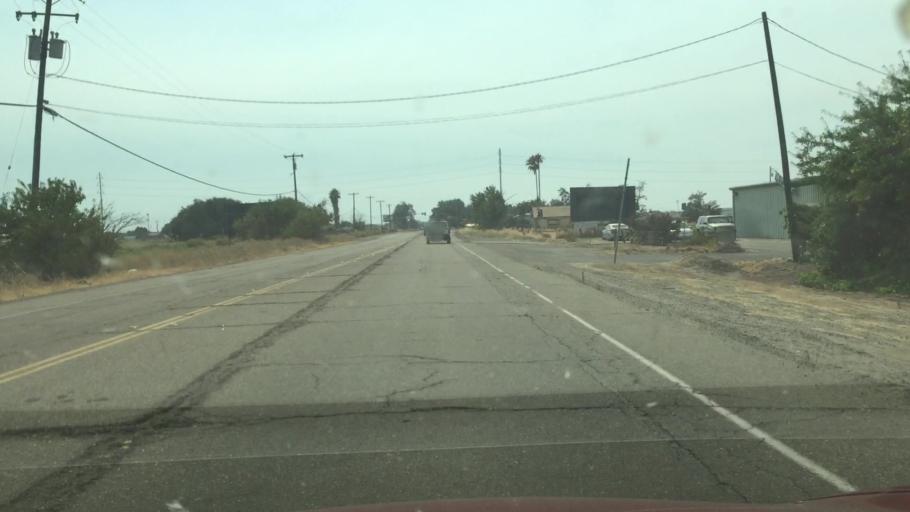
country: US
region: California
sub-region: San Joaquin County
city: Lathrop
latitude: 37.7964
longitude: -121.2742
